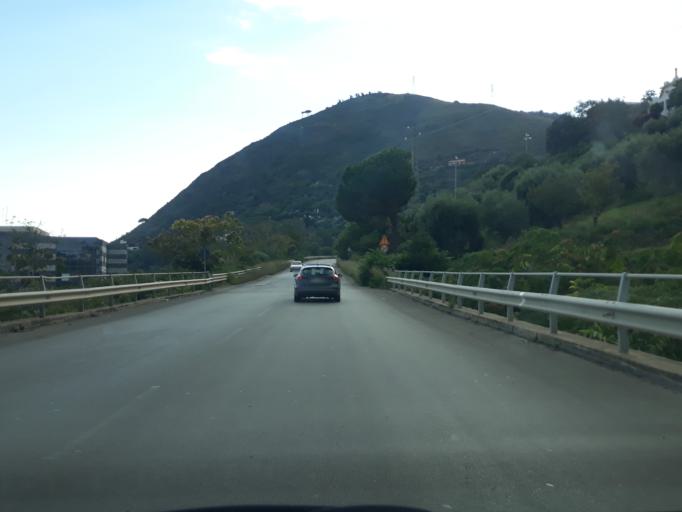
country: IT
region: Sicily
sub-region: Palermo
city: Cefalu
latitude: 38.0276
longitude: 14.0103
